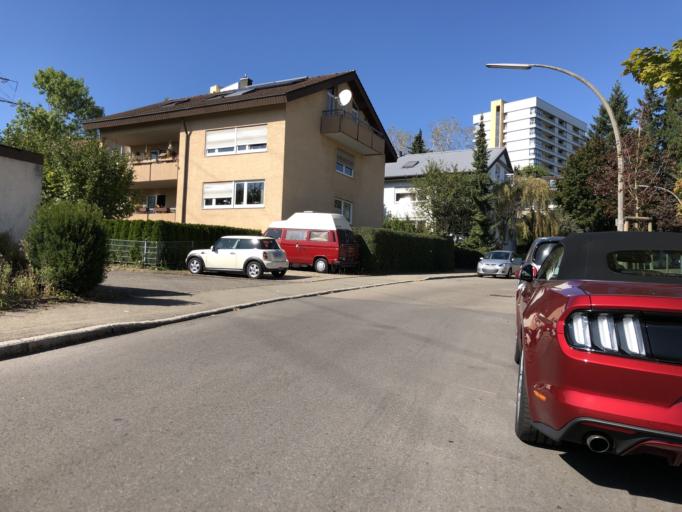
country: DE
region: Baden-Wuerttemberg
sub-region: Regierungsbezirk Stuttgart
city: Sindelfingen
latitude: 48.7185
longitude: 9.0008
